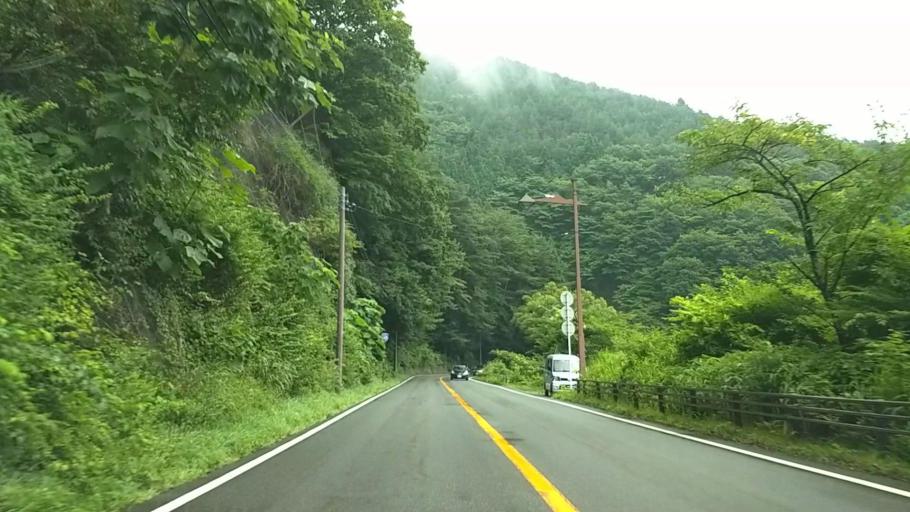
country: JP
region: Yamanashi
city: Fujikawaguchiko
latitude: 35.4886
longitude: 138.6138
